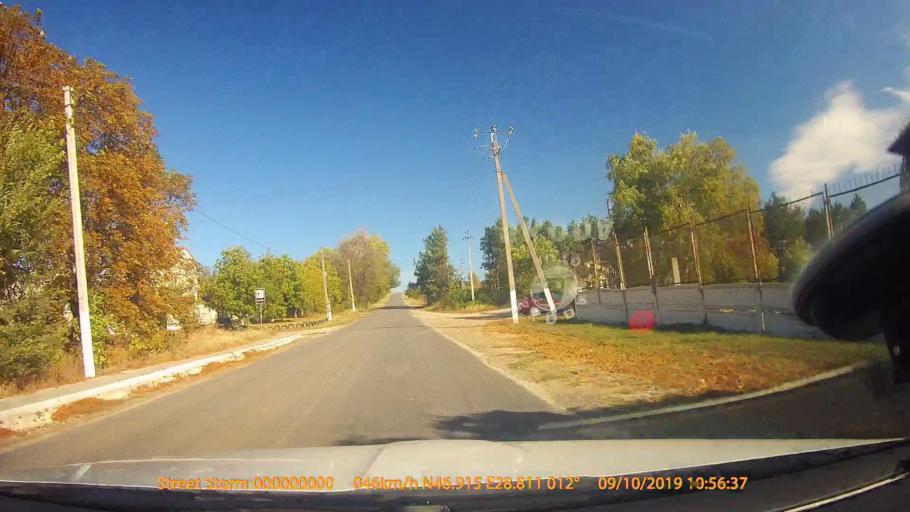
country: MD
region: Laloveni
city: Ialoveni
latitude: 46.9149
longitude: 28.8111
